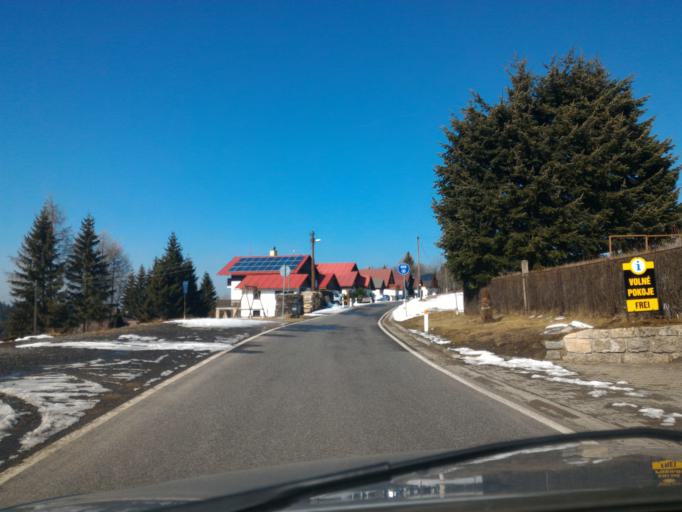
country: CZ
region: Liberecky
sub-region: Okres Jablonec nad Nisou
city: Korenov
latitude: 50.7556
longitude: 15.3589
